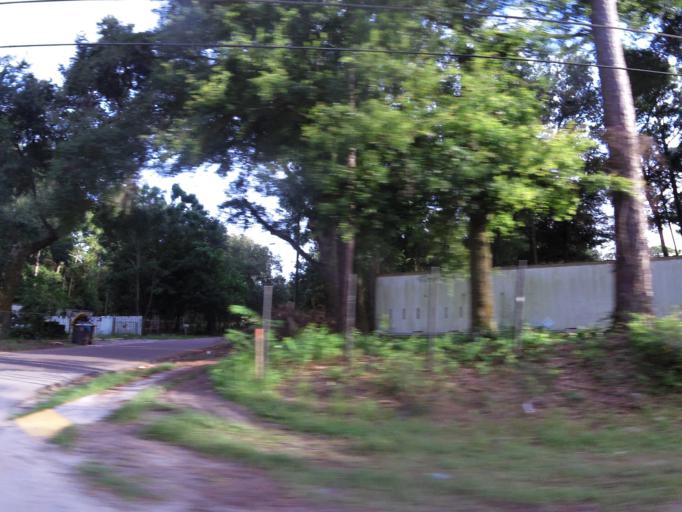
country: US
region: Florida
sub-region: Duval County
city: Jacksonville
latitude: 30.4170
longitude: -81.7203
